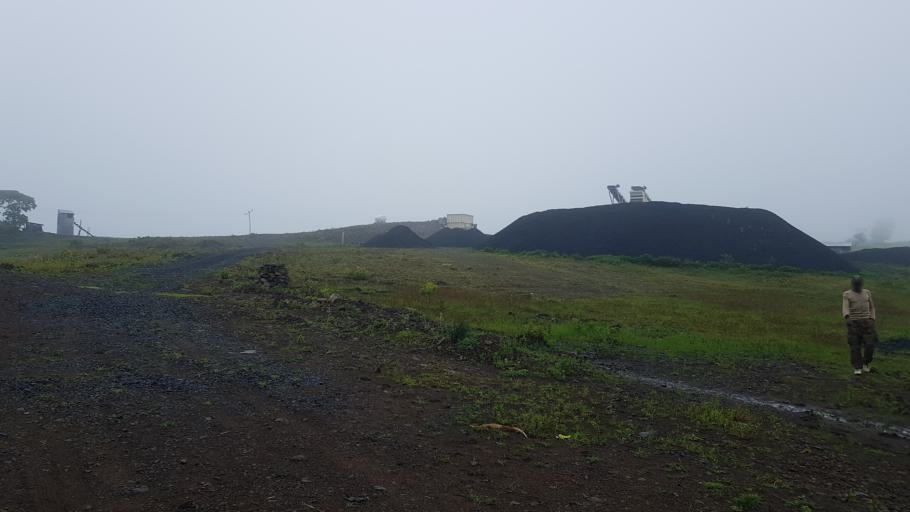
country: ET
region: Oromiya
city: Metahara
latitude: 8.5120
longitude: 40.0319
